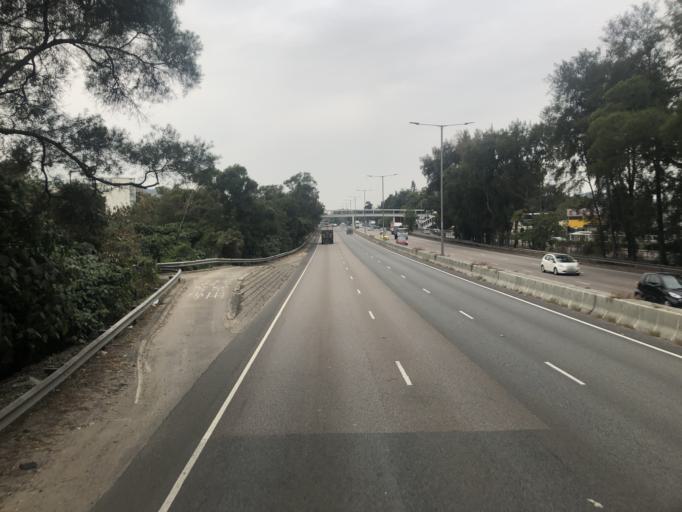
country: CN
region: Guangdong
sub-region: Shenzhen
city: Shenzhen
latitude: 22.5021
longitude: 114.1140
